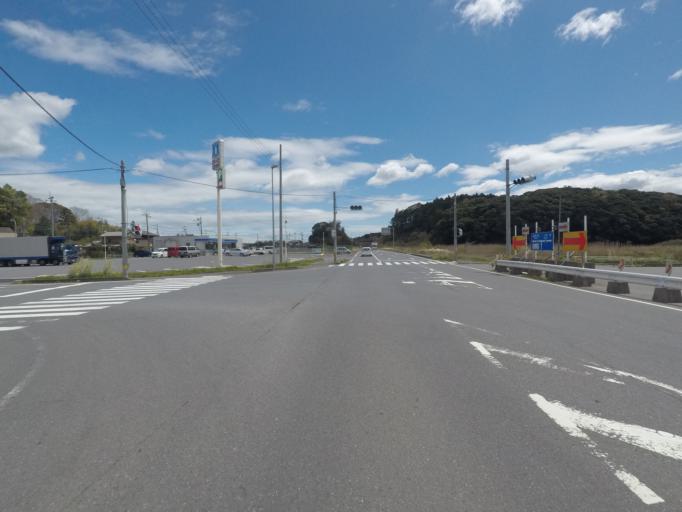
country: JP
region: Ibaraki
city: Itako
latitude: 36.0931
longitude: 140.5167
